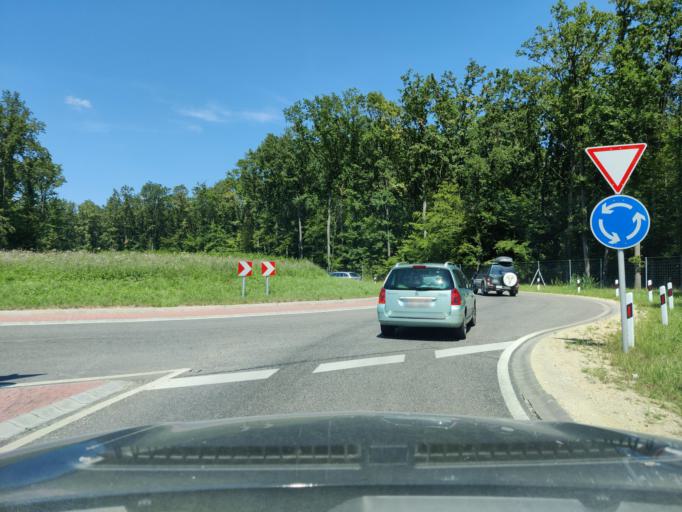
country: HU
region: Vas
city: Kormend
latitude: 47.0269
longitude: 16.6150
